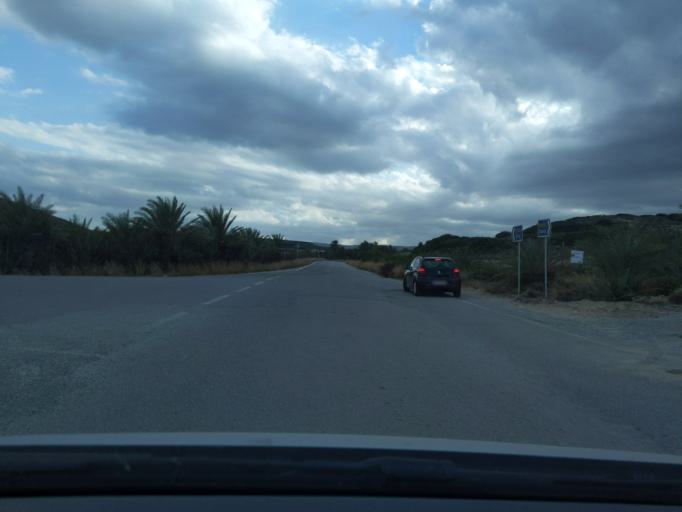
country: GR
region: Crete
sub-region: Nomos Lasithiou
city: Palekastro
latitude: 35.2541
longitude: 26.2532
